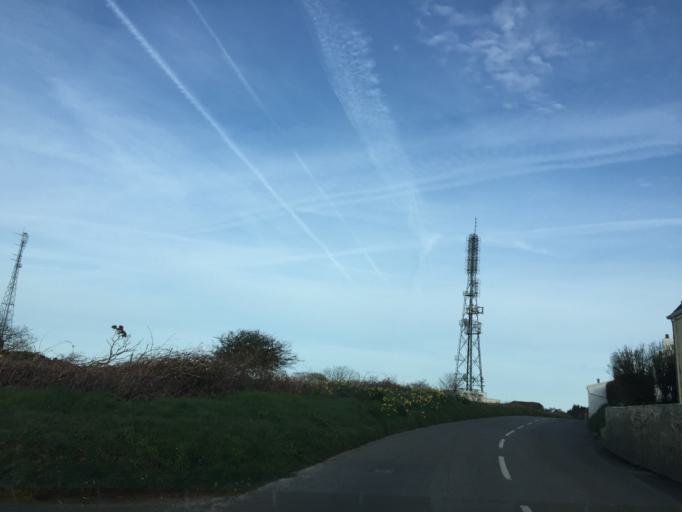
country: JE
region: St Helier
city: Saint Helier
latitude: 49.2463
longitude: -2.1037
